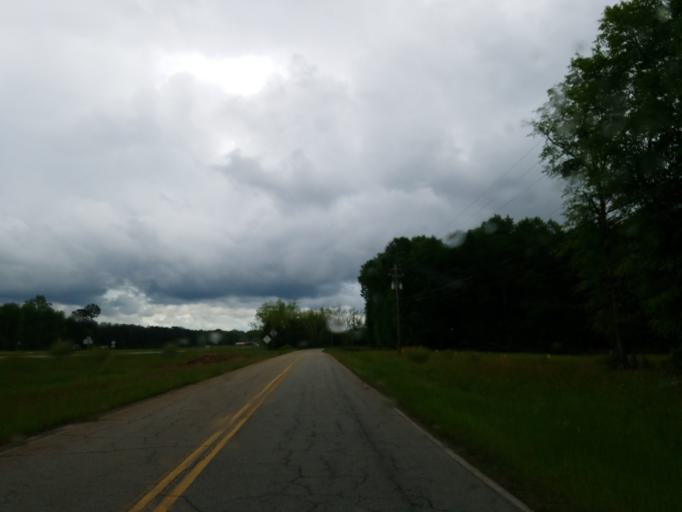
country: US
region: Georgia
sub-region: Lamar County
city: Barnesville
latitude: 33.1023
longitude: -84.1873
